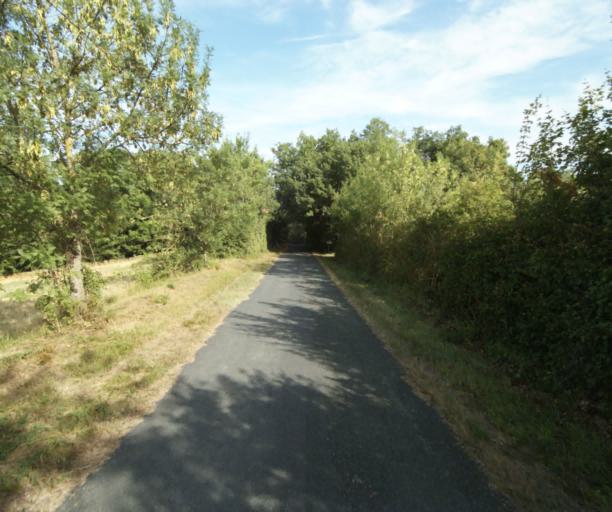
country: FR
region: Midi-Pyrenees
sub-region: Departement du Tarn
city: Soual
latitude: 43.5294
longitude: 2.0704
